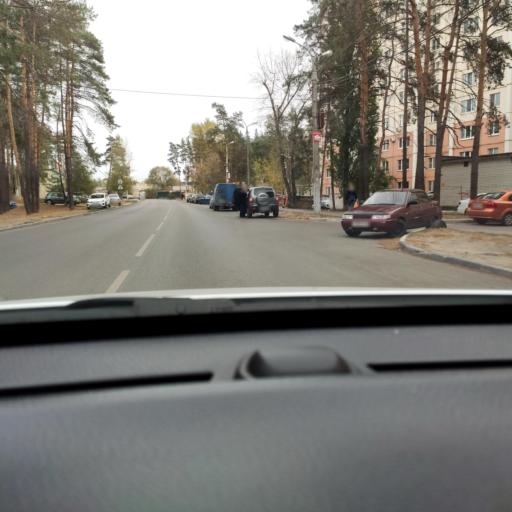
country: RU
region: Voronezj
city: Pridonskoy
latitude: 51.6810
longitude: 39.0921
